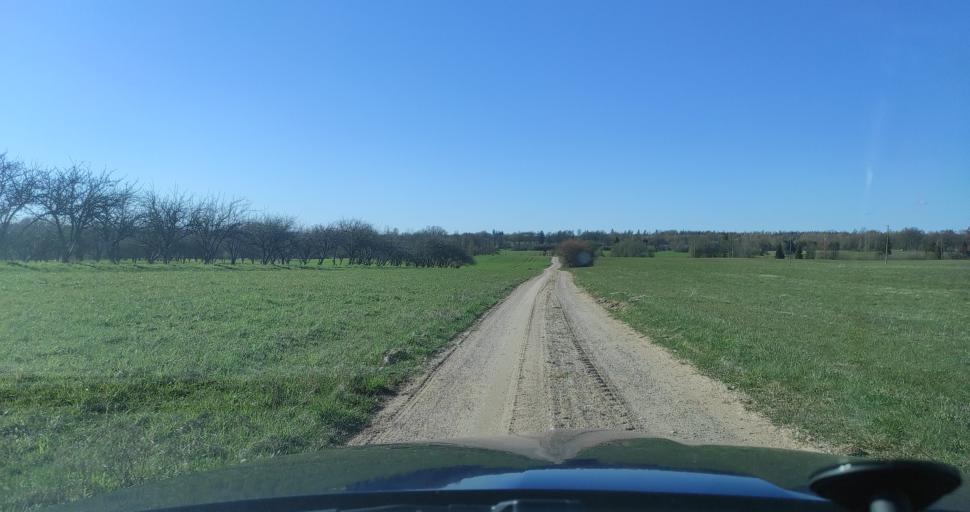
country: LV
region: Kuldigas Rajons
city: Kuldiga
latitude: 56.8708
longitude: 21.8402
